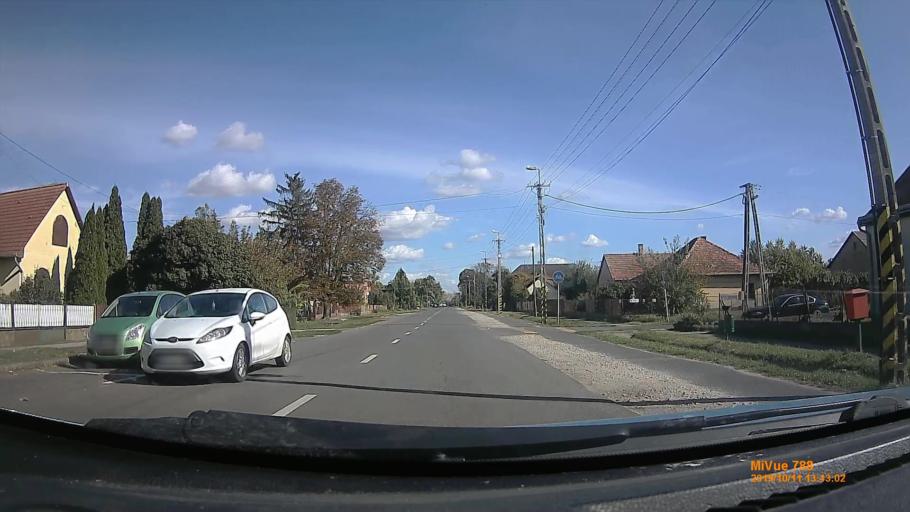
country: HU
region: Hajdu-Bihar
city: Balmazujvaros
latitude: 47.5390
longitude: 21.3482
